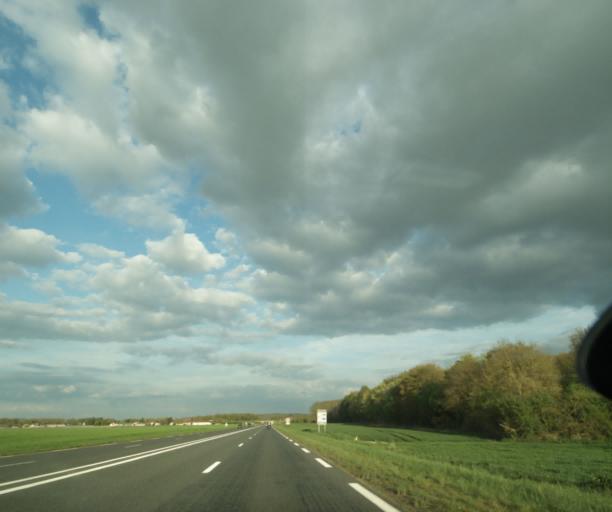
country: FR
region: Ile-de-France
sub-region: Departement de Seine-et-Marne
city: Barbizon
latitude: 48.4567
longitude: 2.5933
